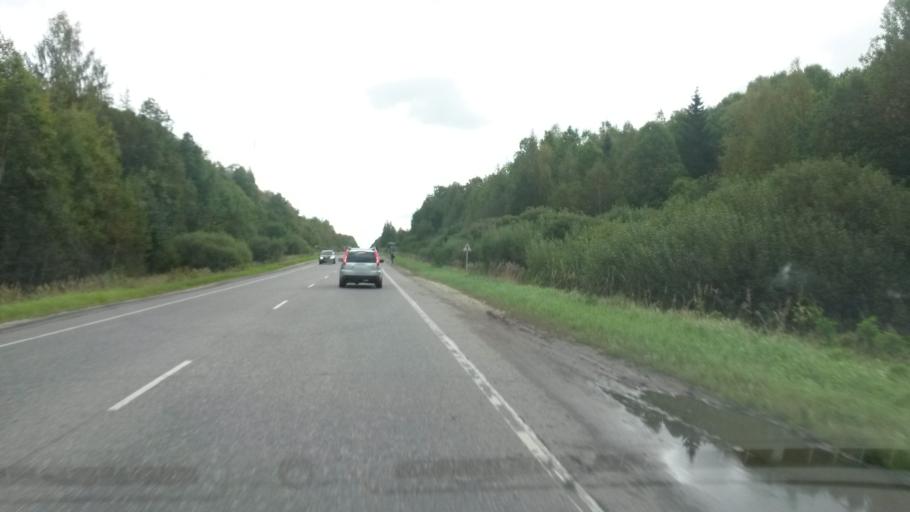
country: RU
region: Ivanovo
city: Rodniki
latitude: 57.0882
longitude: 41.6751
